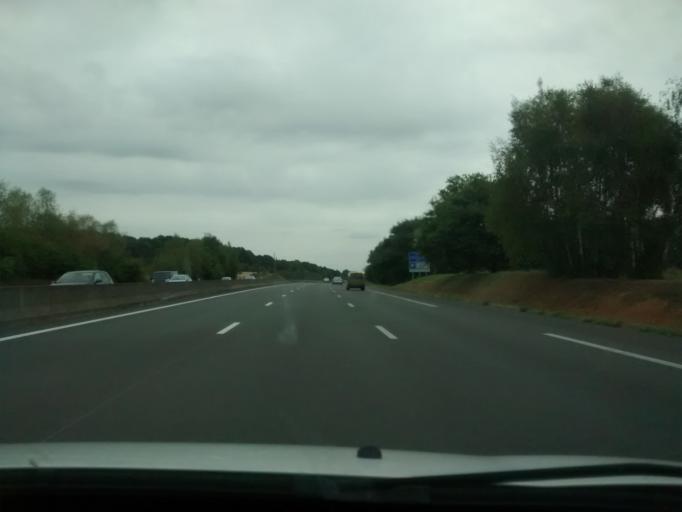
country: FR
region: Centre
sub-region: Departement d'Eure-et-Loir
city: Authon-du-Perche
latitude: 48.2096
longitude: 0.9315
